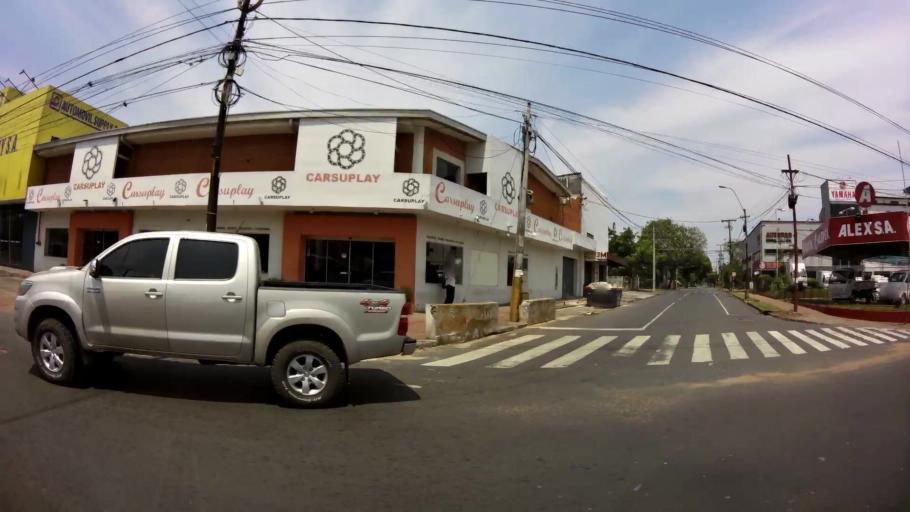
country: PY
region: Central
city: Fernando de la Mora
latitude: -25.3197
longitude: -57.5625
